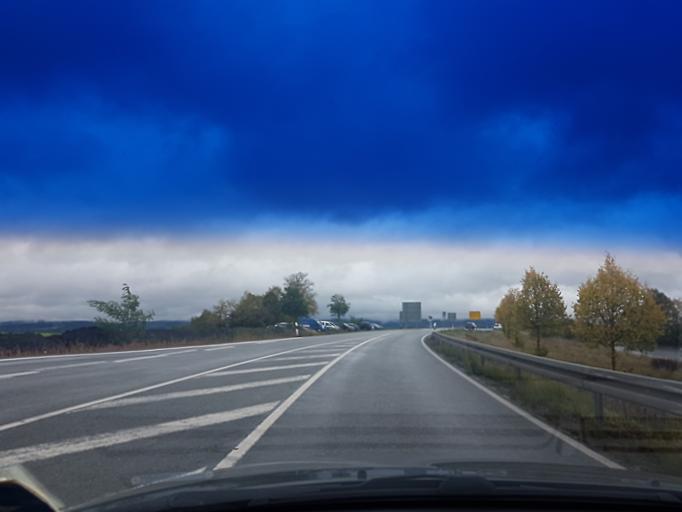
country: DE
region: Bavaria
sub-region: Upper Franconia
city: Bindlach
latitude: 50.0149
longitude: 11.6074
